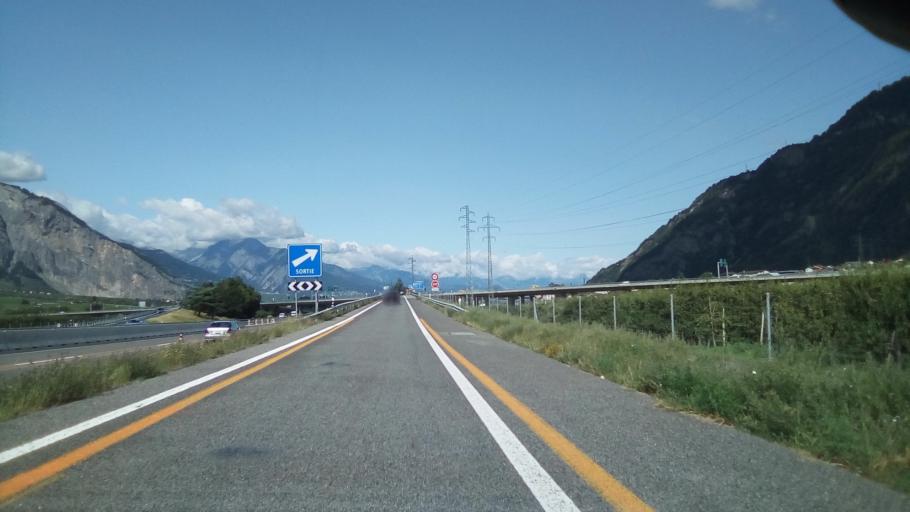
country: CH
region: Valais
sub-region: Martigny District
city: Riddes
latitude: 46.1701
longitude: 7.2109
